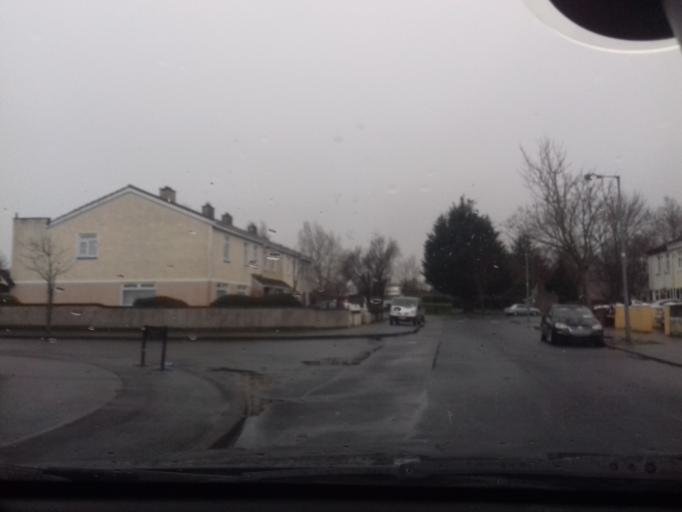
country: IE
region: Leinster
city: Hartstown
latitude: 53.3918
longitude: -6.4067
